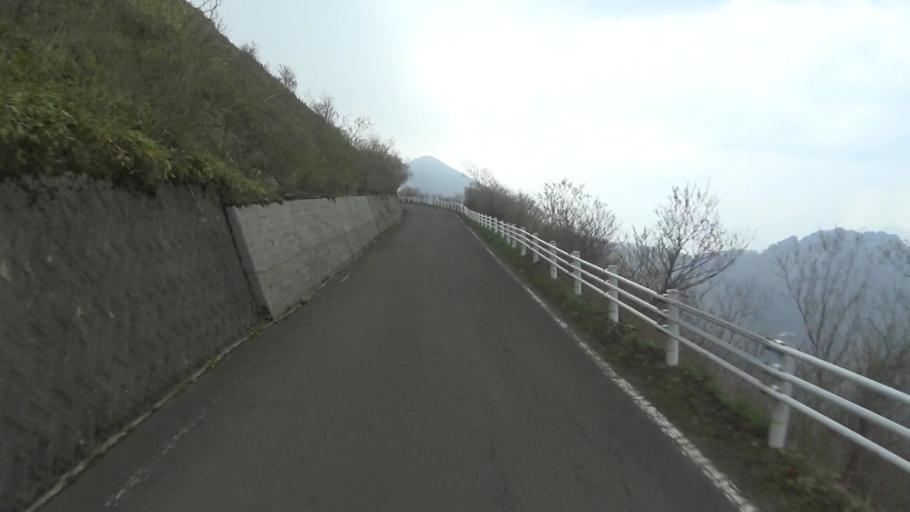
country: JP
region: Ehime
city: Saijo
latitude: 33.7794
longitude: 133.2230
